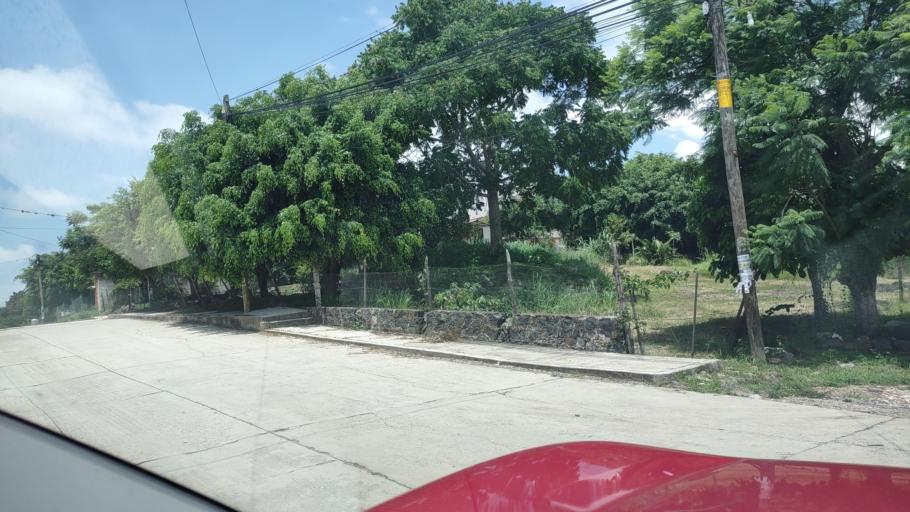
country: MX
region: Veracruz
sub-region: Emiliano Zapata
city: Dos Rios
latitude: 19.4900
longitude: -96.8137
